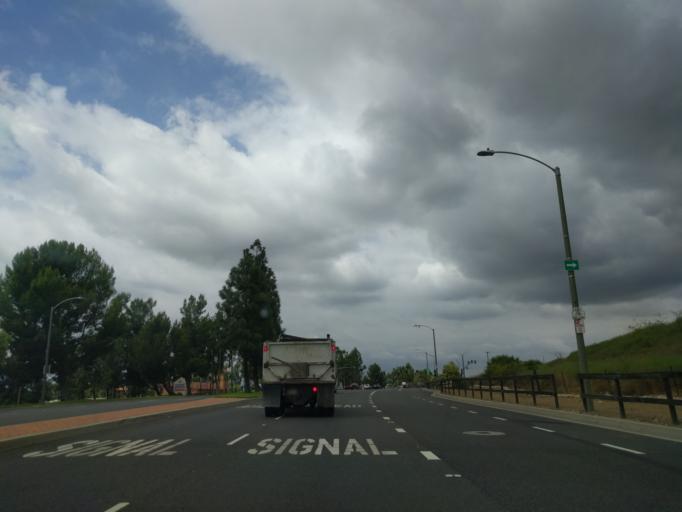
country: US
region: California
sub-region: Orange County
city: North Tustin
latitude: 33.7905
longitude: -117.7612
